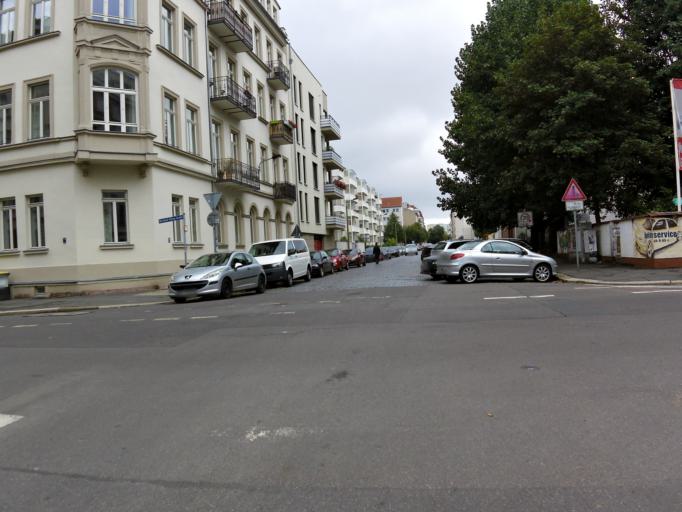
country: DE
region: Saxony
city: Leipzig
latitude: 51.3268
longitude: 12.3770
